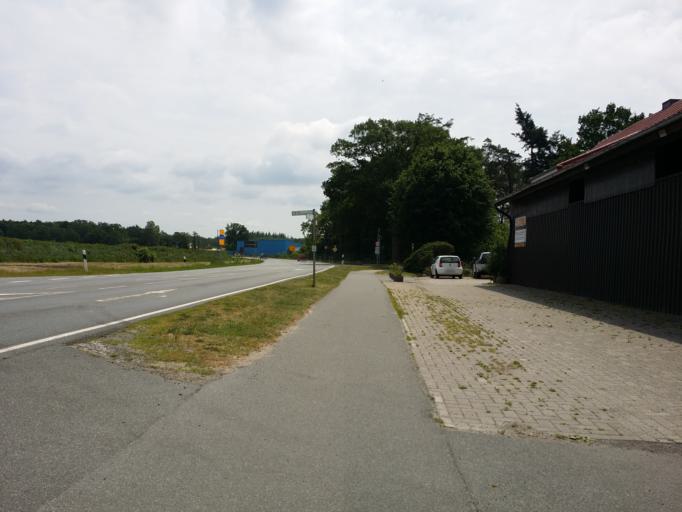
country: DE
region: Lower Saxony
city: Friedeburg
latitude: 53.4112
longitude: 7.8927
